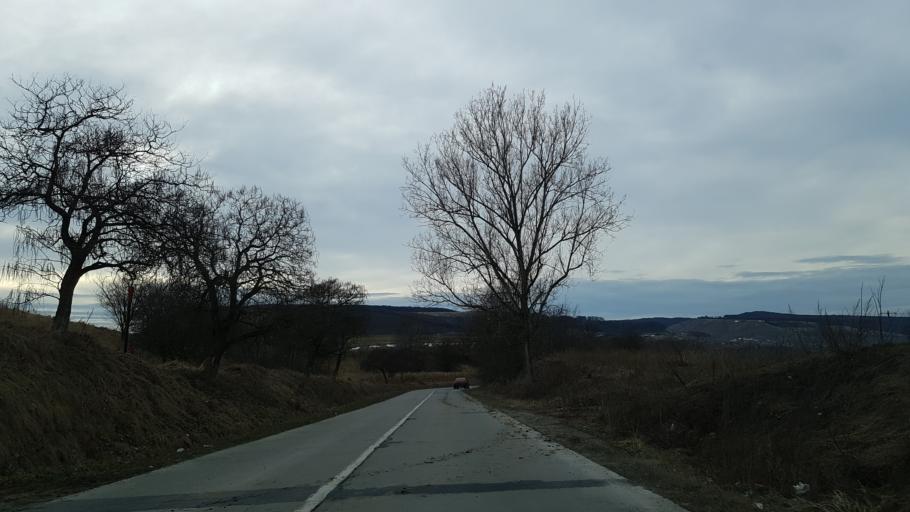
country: RO
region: Sibiu
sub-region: Comuna Micasasa
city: Micasasa
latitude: 46.0746
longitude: 24.1003
